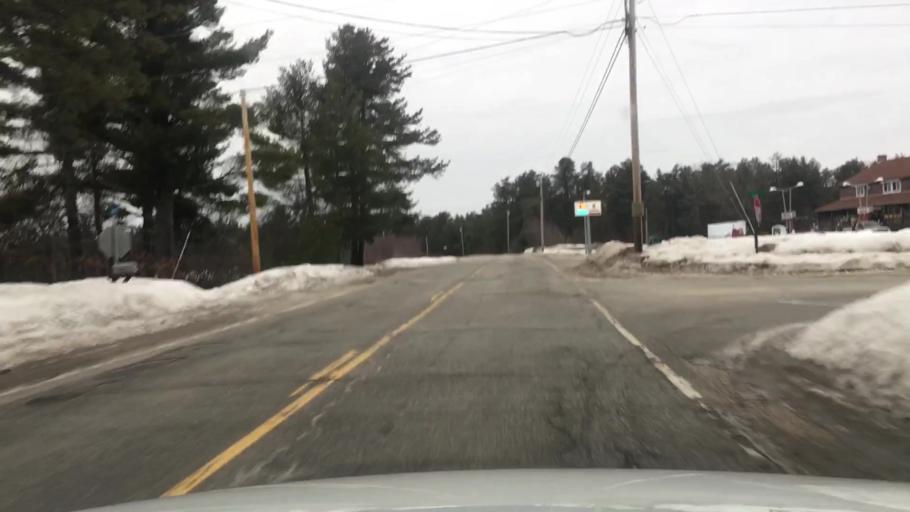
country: US
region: Maine
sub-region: York County
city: Shapleigh
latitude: 43.5659
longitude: -70.8587
